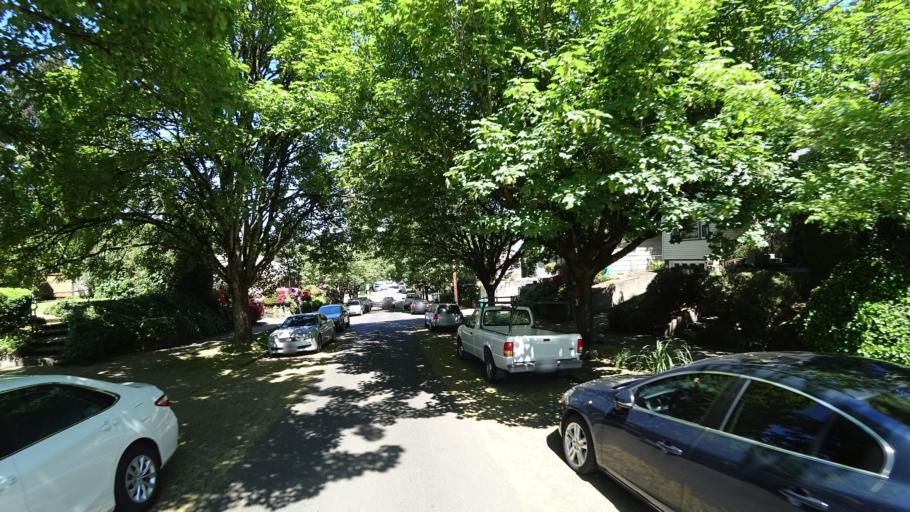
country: US
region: Oregon
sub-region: Multnomah County
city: Portland
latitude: 45.5029
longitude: -122.6326
